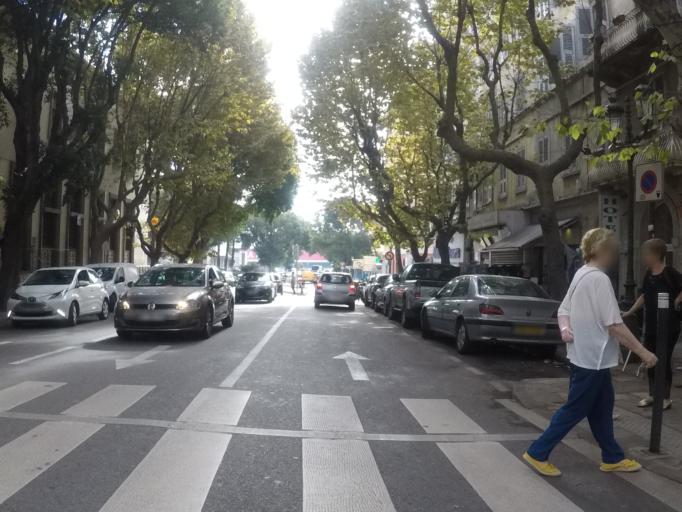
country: FR
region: Corsica
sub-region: Departement de la Haute-Corse
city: Bastia
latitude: 42.7022
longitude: 9.4499
